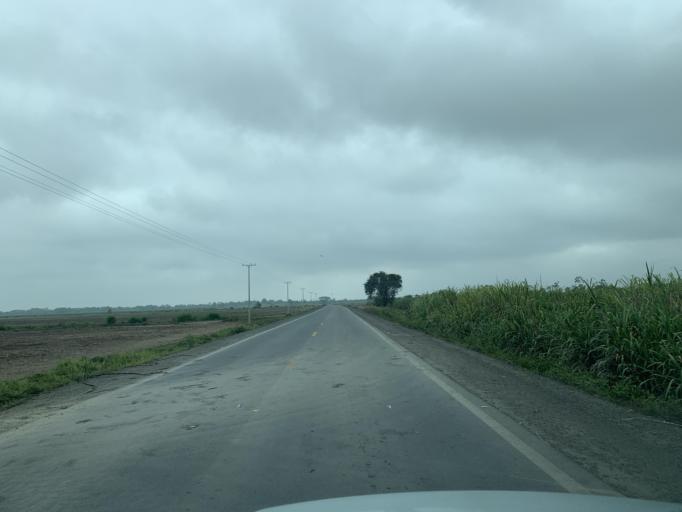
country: EC
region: Guayas
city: Coronel Marcelino Mariduena
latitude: -2.3113
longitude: -79.5114
